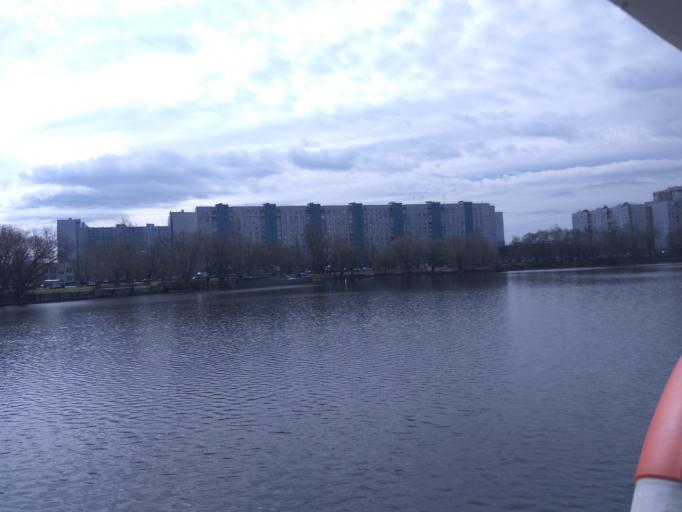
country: RU
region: Moscow
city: Kolomenskoye
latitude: 55.6820
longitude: 37.6985
